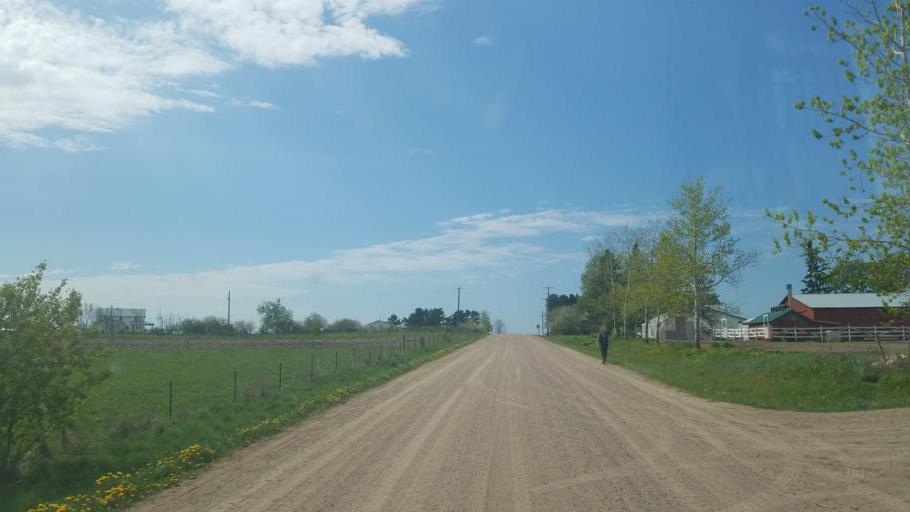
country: US
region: Wisconsin
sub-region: Marathon County
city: Spencer
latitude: 44.5994
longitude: -90.3764
